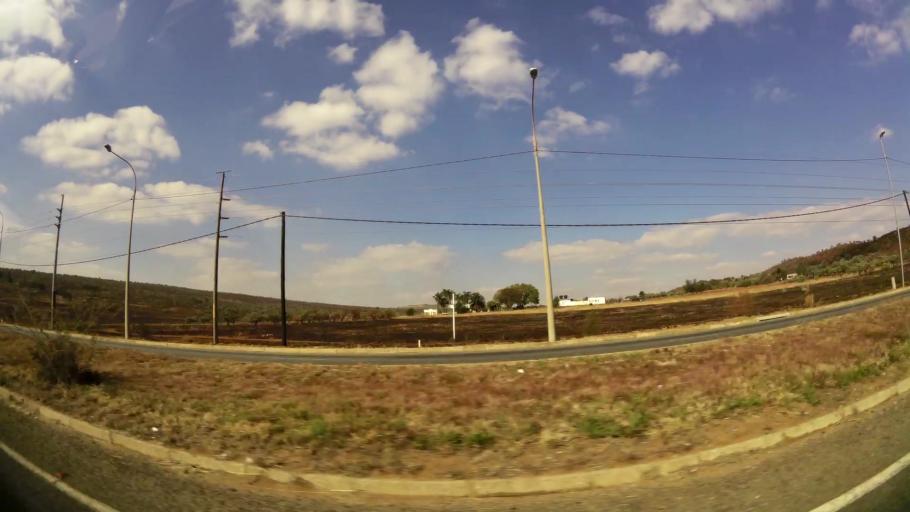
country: ZA
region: Gauteng
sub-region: West Rand District Municipality
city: Krugersdorp
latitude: -26.0696
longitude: 27.8028
